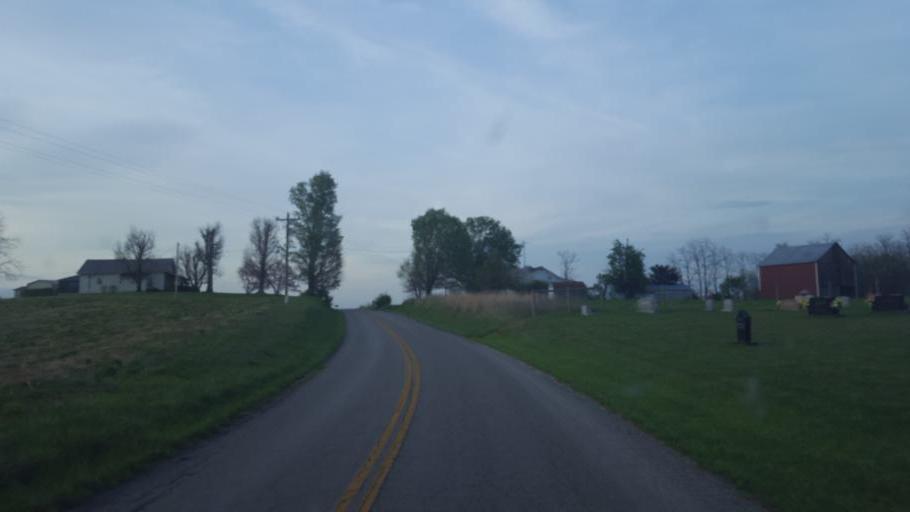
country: US
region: Kentucky
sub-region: Metcalfe County
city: Edmonton
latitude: 37.1253
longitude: -85.6955
